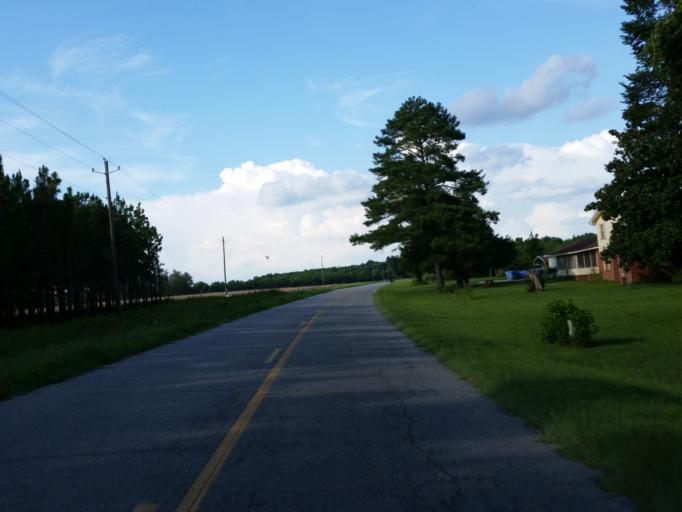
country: US
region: Georgia
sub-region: Dooly County
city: Vienna
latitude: 32.0738
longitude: -83.8122
